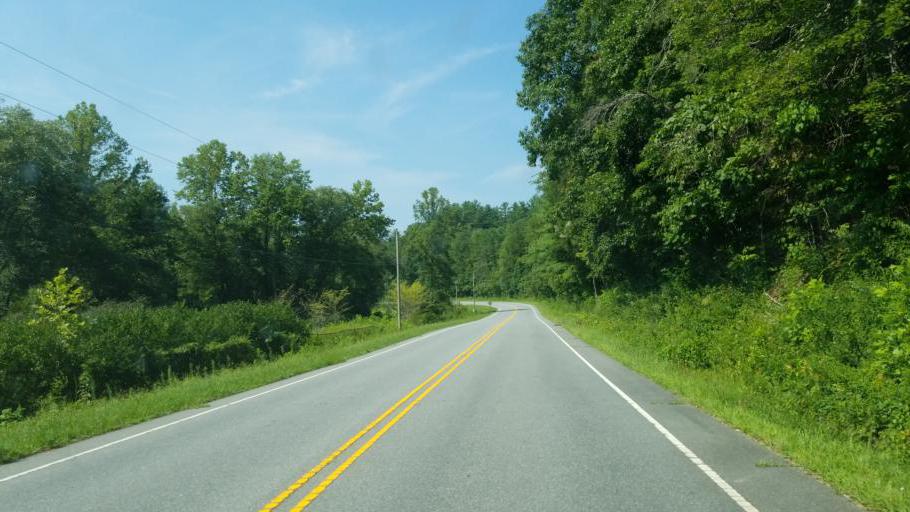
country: US
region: North Carolina
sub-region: Burke County
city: Glen Alpine
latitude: 35.8451
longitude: -81.7741
